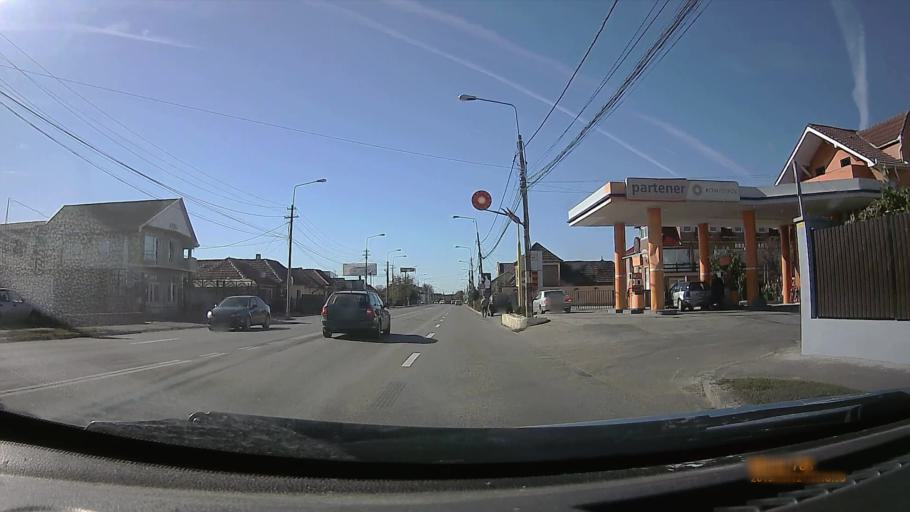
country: RO
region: Bihor
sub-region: Comuna Sanmartin
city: Sanmartin
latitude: 47.0366
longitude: 21.9930
